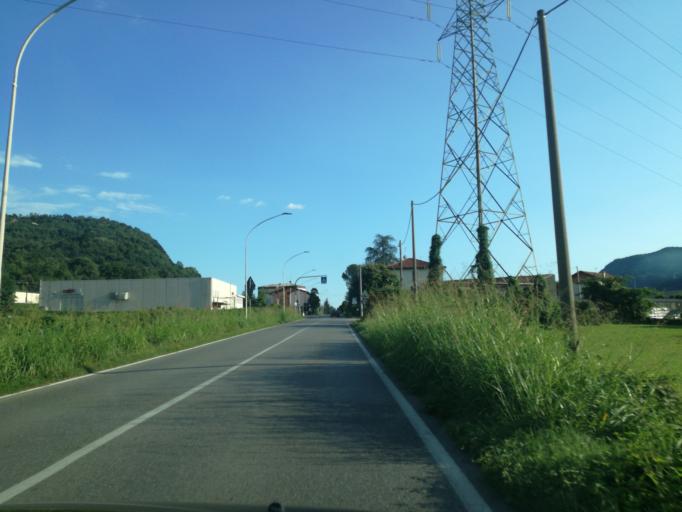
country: IT
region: Lombardy
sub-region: Provincia di Lecco
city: Calolziocorte
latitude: 45.7828
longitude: 9.4413
